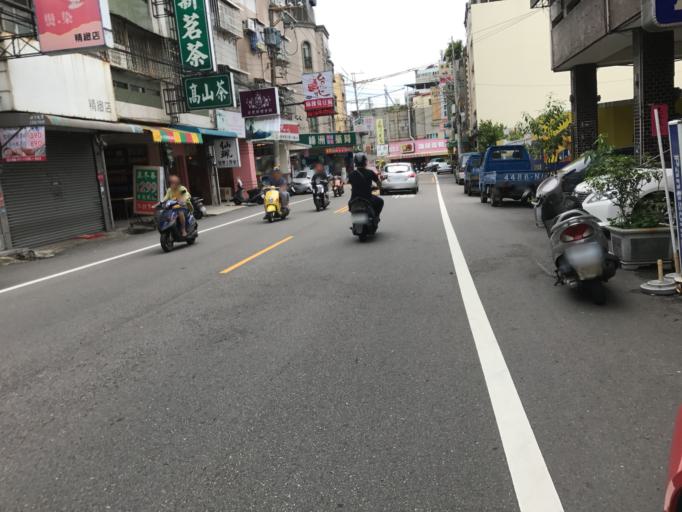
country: TW
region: Taiwan
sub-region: Taichung City
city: Taichung
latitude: 24.0880
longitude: 120.7043
